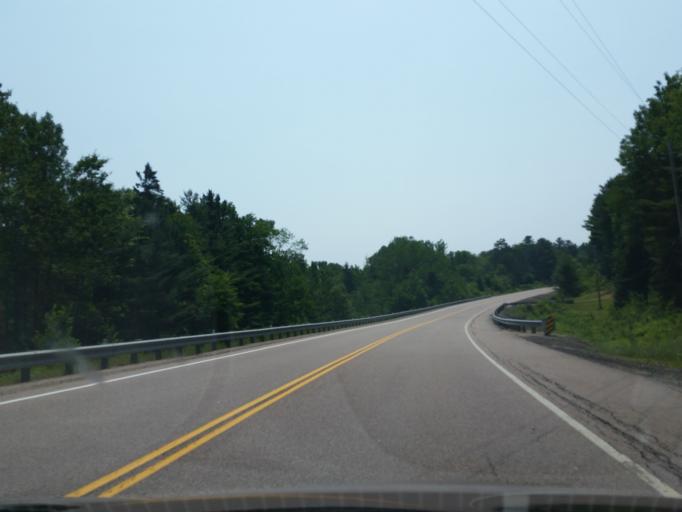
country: CA
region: Ontario
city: Deep River
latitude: 46.2092
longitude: -77.8872
